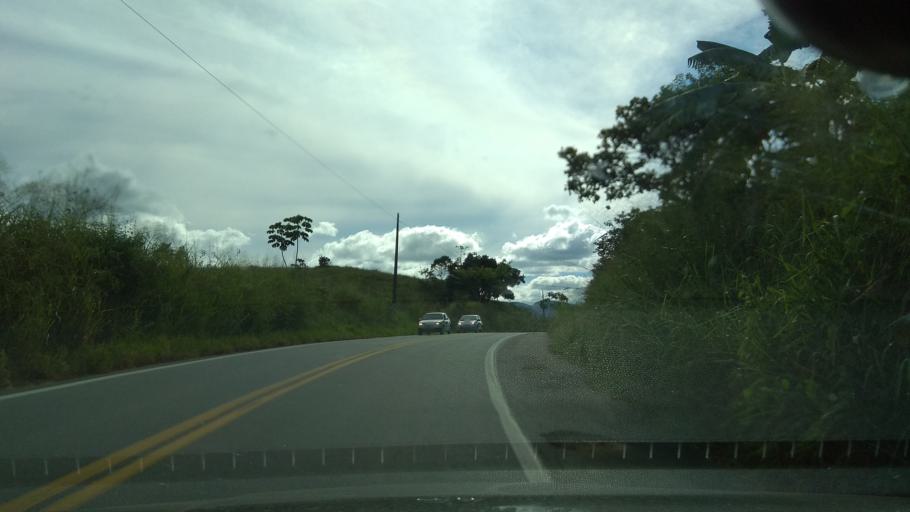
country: BR
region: Bahia
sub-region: Jitauna
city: Jitauna
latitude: -14.0088
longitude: -39.9091
